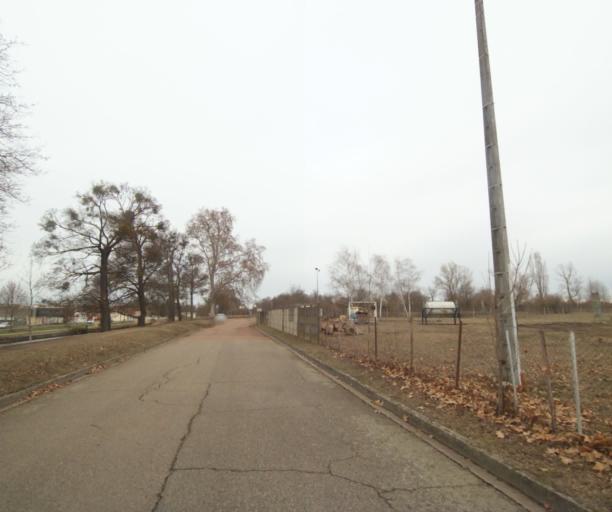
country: FR
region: Rhone-Alpes
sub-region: Departement de la Loire
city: Le Coteau
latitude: 46.0431
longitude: 4.0866
